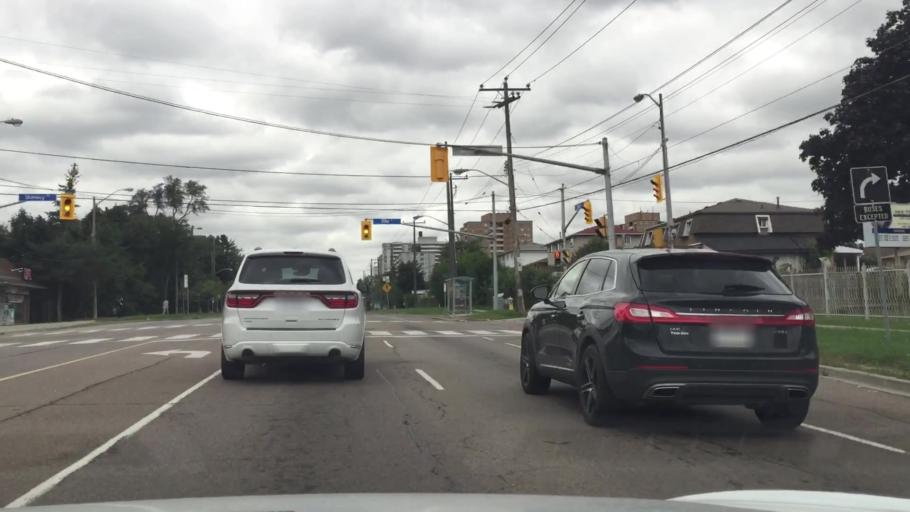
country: CA
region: Ontario
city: Concord
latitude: 43.7428
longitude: -79.5140
